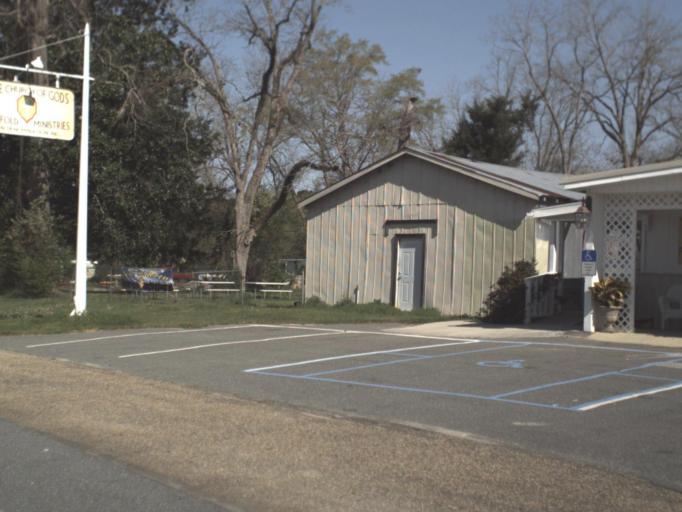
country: US
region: Florida
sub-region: Jackson County
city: Graceville
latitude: 30.9492
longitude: -85.3959
